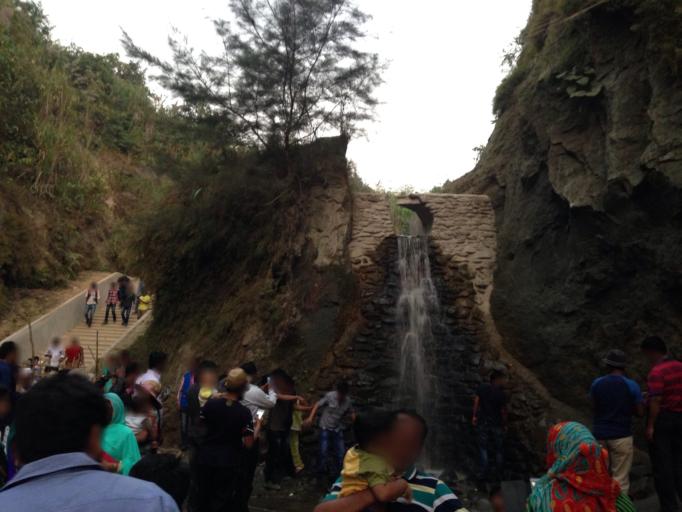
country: BD
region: Chittagong
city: Cox's Bazar
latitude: 21.3550
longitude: 92.0258
